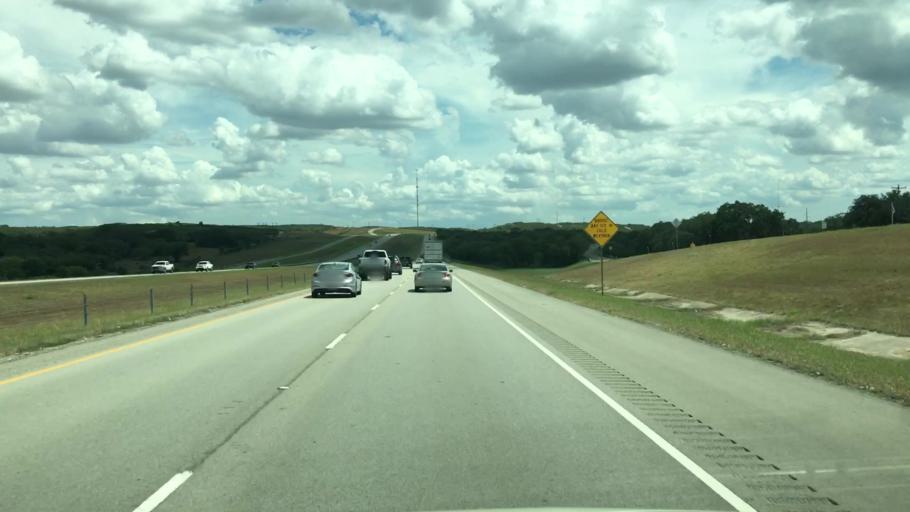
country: US
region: Texas
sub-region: Live Oak County
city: George West
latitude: 28.2635
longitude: -97.9335
